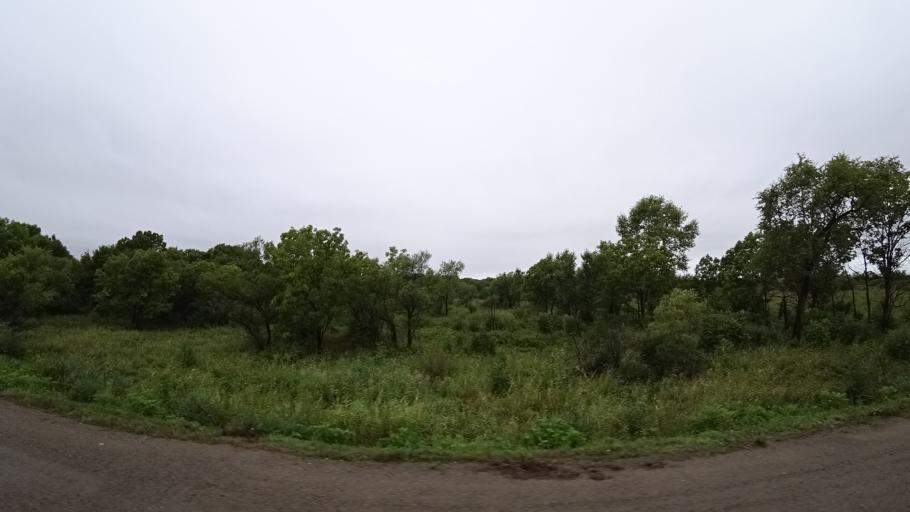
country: RU
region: Primorskiy
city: Monastyrishche
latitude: 44.2183
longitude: 132.4512
